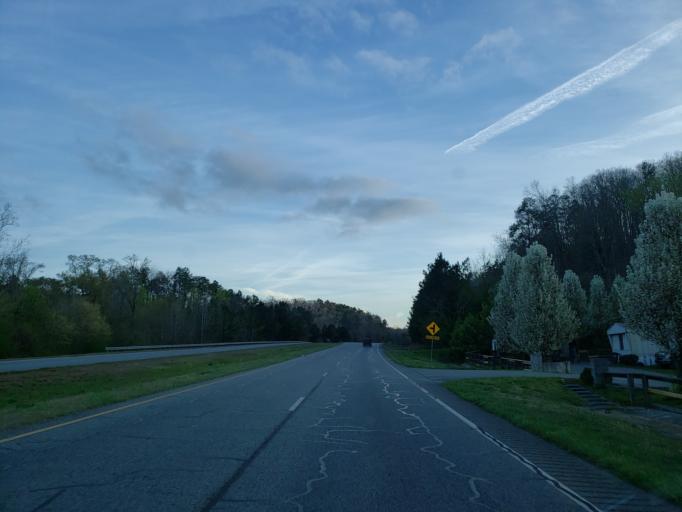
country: US
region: Georgia
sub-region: Polk County
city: Aragon
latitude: 34.0558
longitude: -84.9937
